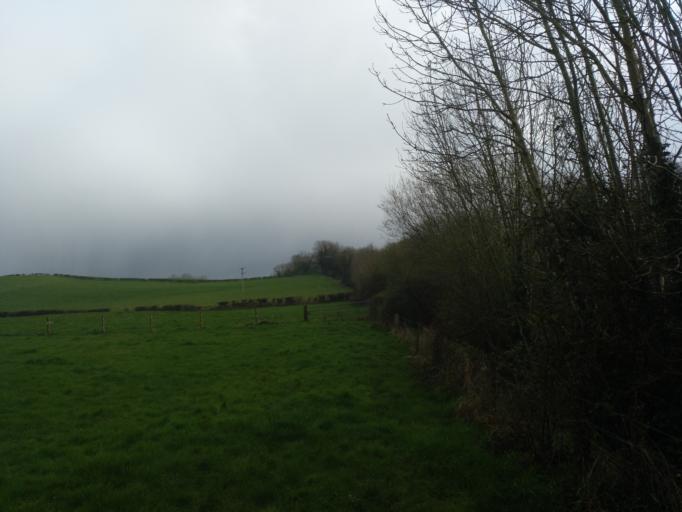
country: IE
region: Ulster
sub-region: County Monaghan
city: Clones
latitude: 54.1862
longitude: -7.1796
